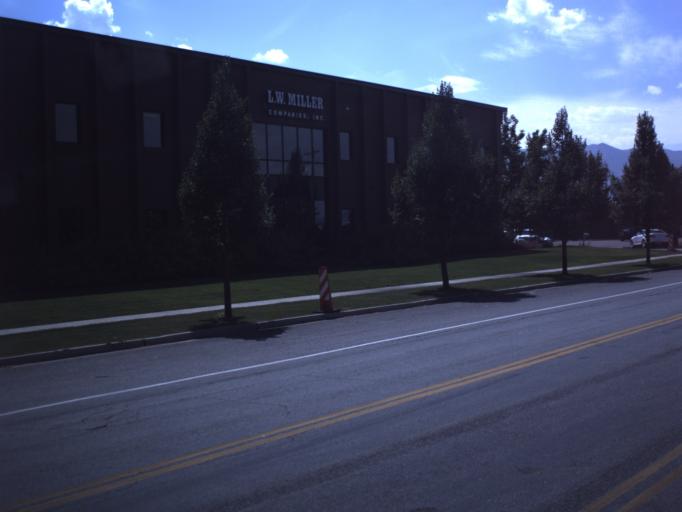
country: US
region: Utah
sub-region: Cache County
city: Logan
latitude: 41.7357
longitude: -111.8611
